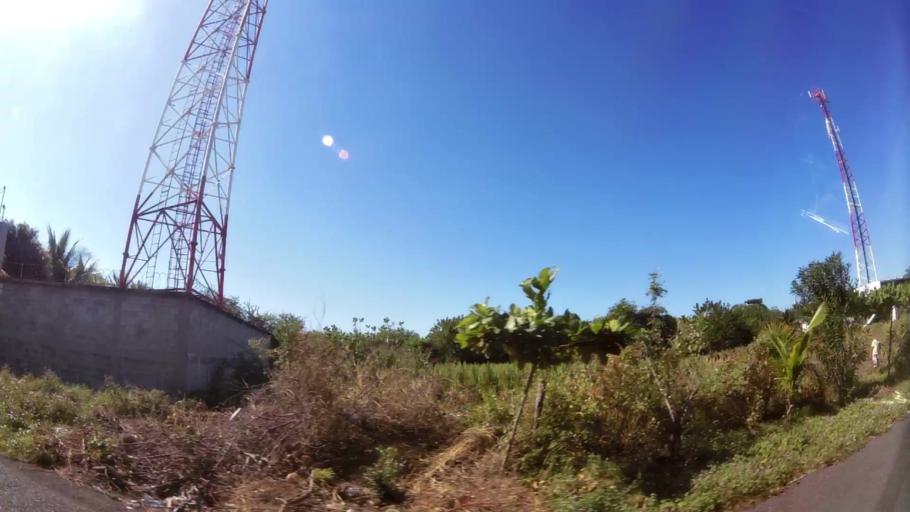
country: GT
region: Santa Rosa
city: Guazacapan
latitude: 13.8676
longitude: -90.4132
